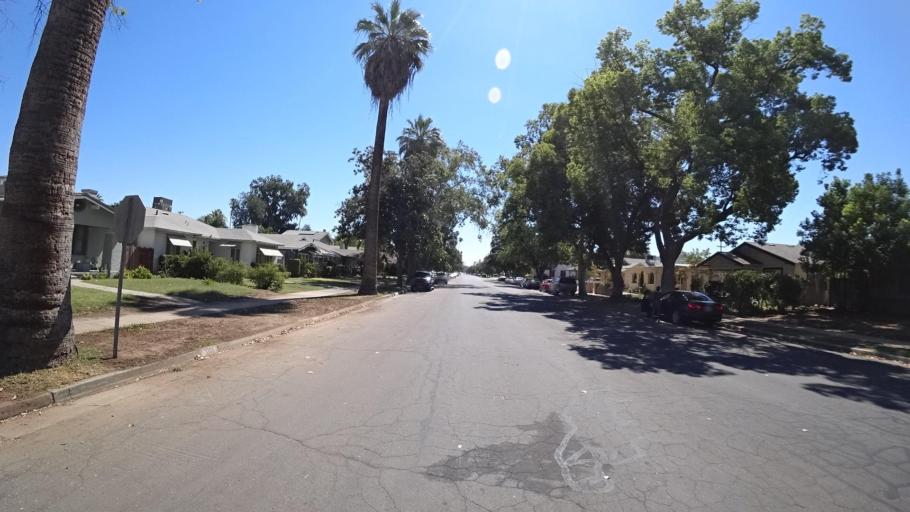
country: US
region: California
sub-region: Fresno County
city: Fresno
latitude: 36.7381
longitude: -119.7691
